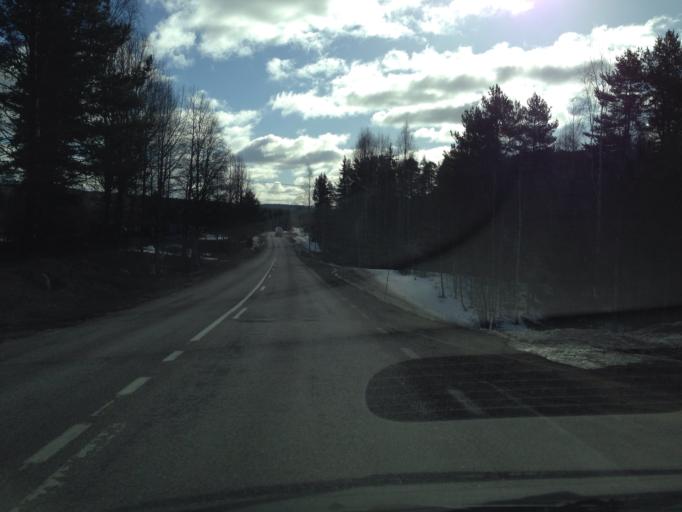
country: SE
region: Gaevleborg
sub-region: Ljusdals Kommun
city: Farila
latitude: 61.9811
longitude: 15.3174
